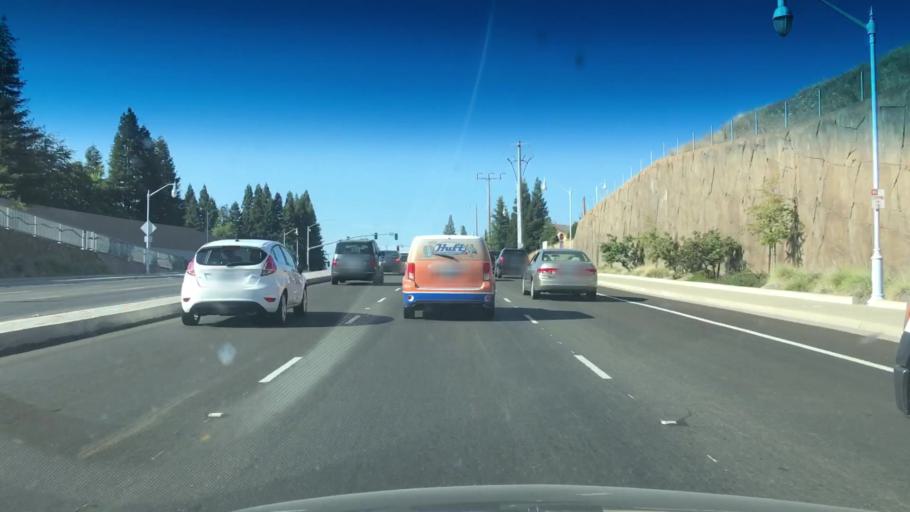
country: US
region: California
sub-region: Sacramento County
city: Gold River
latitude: 38.6386
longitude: -121.2255
